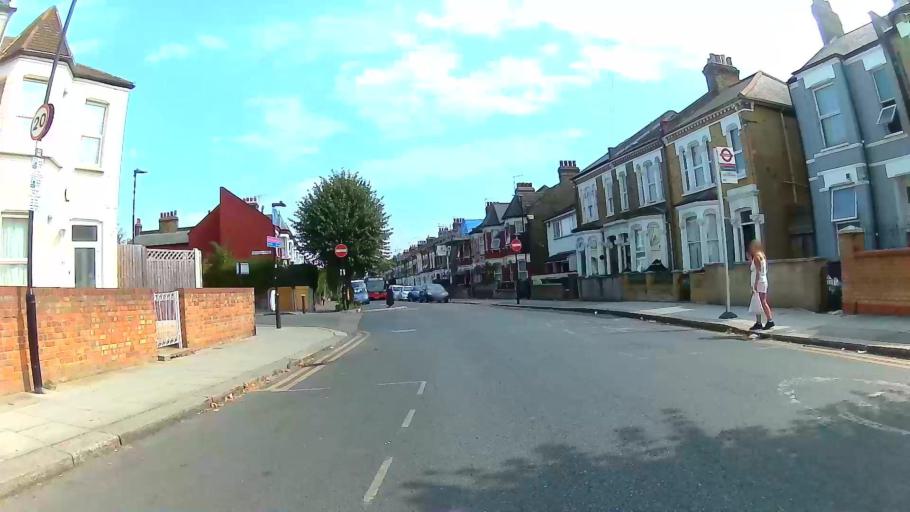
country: GB
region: England
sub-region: Greater London
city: Harringay
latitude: 51.5942
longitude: -0.0758
